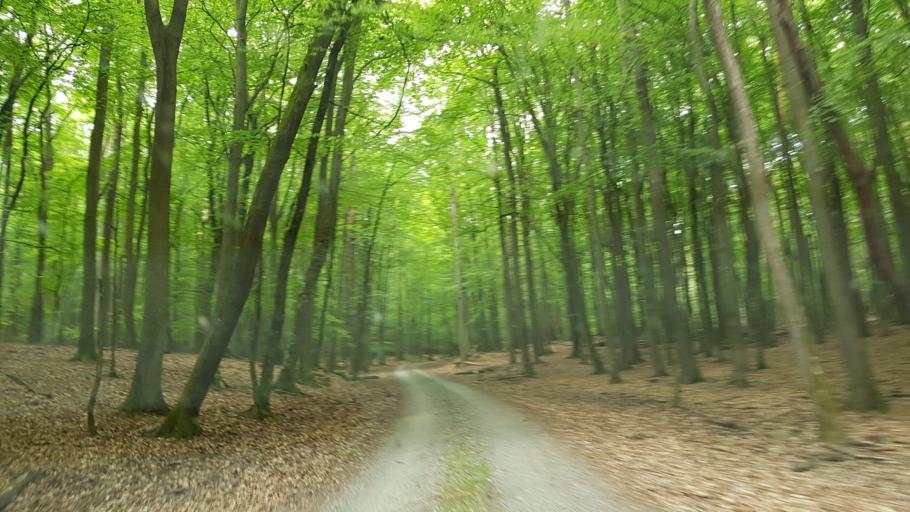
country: PL
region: West Pomeranian Voivodeship
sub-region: Powiat kamienski
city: Miedzyzdroje
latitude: 53.9487
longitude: 14.5504
